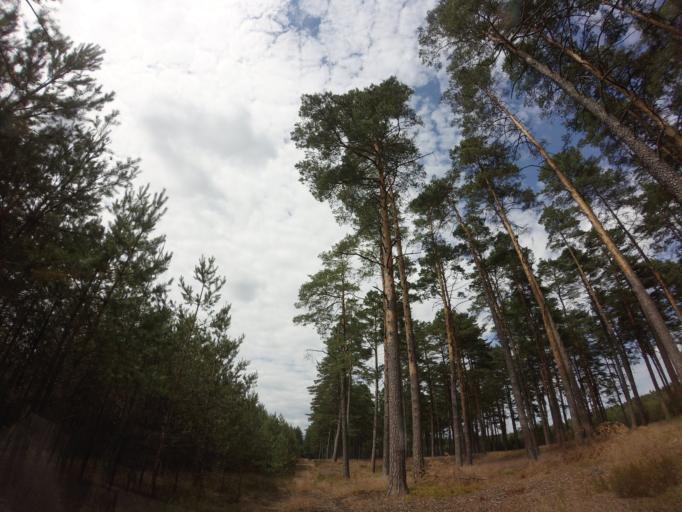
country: PL
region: West Pomeranian Voivodeship
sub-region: Powiat choszczenski
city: Drawno
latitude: 53.1620
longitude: 15.7501
